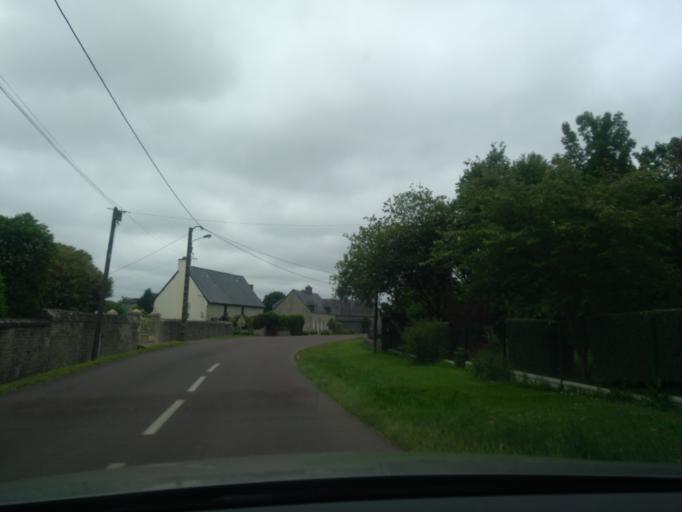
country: FR
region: Lower Normandy
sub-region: Departement de la Manche
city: Sainte-Mere-Eglise
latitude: 49.4287
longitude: -1.3042
